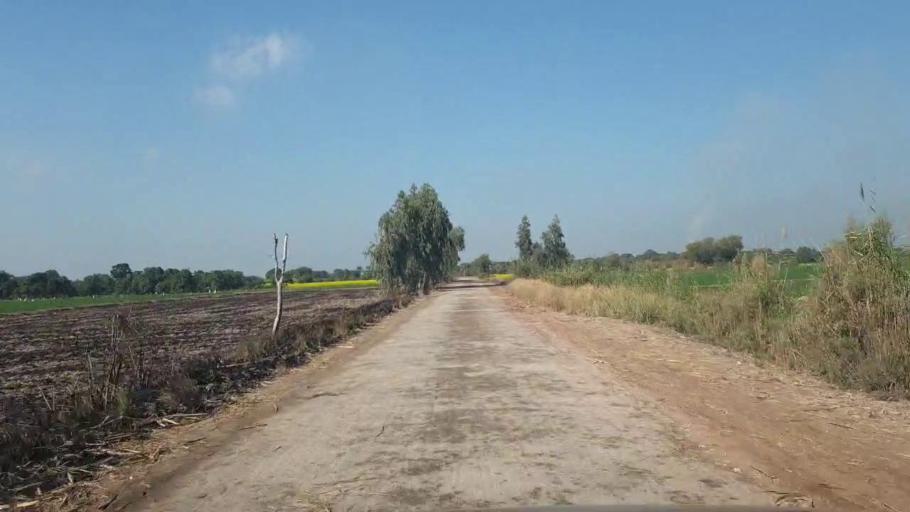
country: PK
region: Sindh
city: Shahdadpur
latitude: 25.9115
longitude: 68.5949
